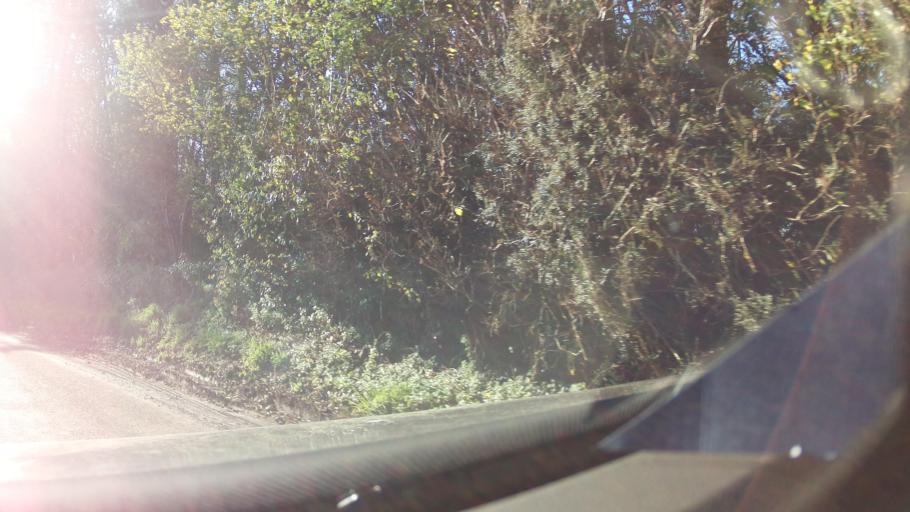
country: GB
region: England
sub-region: Somerset
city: Castle Cary
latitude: 51.0291
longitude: -2.5000
